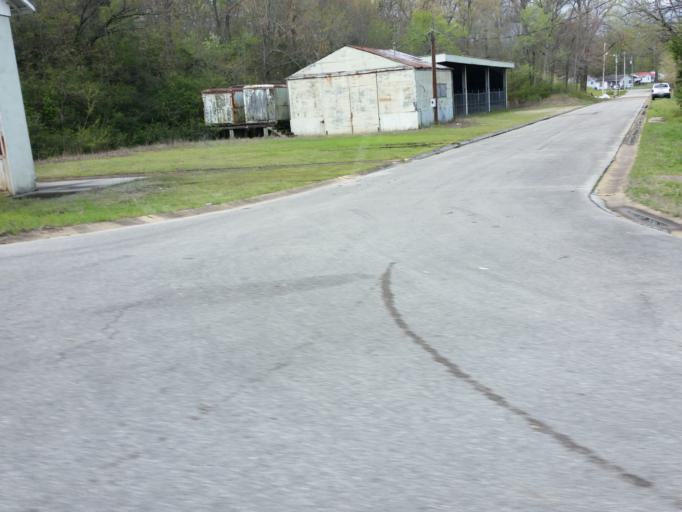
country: US
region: Missouri
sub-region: Butler County
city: Poplar Bluff
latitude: 36.7526
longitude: -90.4003
